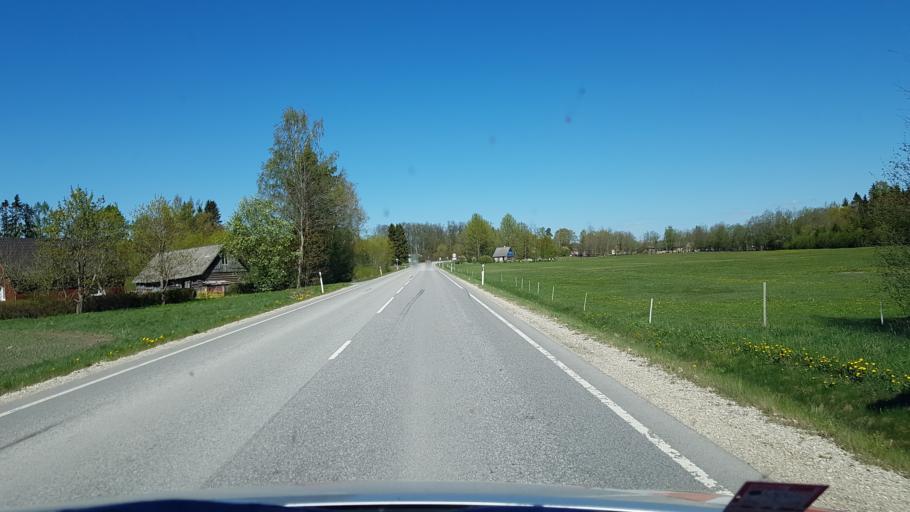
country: EE
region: Jogevamaa
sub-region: Mustvee linn
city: Mustvee
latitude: 59.0102
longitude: 26.7135
